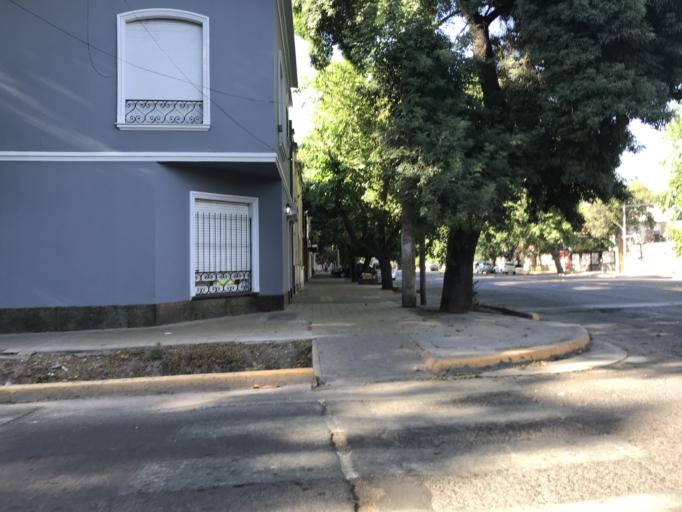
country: AR
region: Mendoza
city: Mendoza
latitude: -32.8807
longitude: -68.8420
